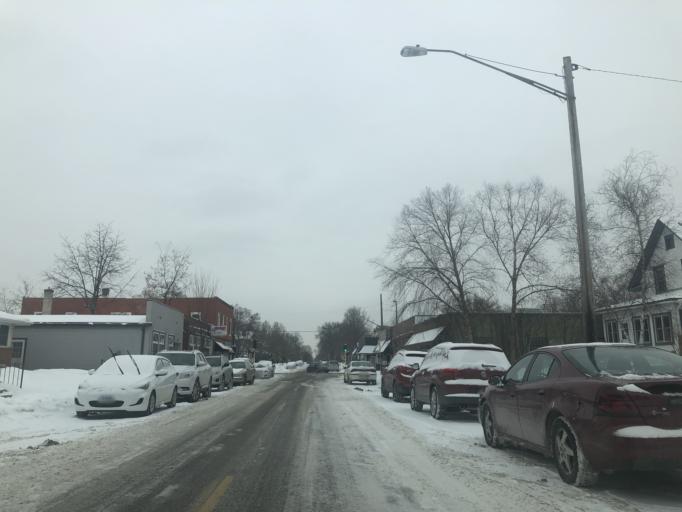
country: US
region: Minnesota
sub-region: Hennepin County
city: Richfield
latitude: 44.9333
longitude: -93.2844
